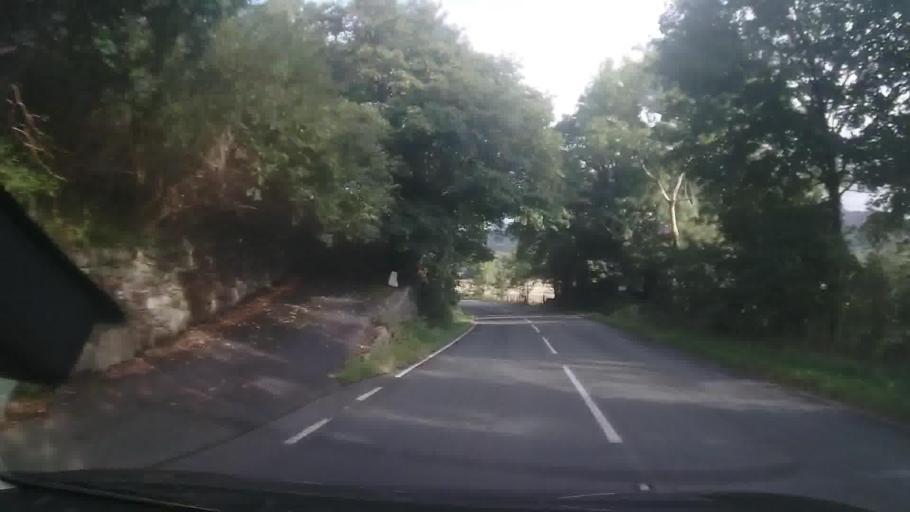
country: GB
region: Wales
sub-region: Gwynedd
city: Barmouth
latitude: 52.7432
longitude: -3.9976
